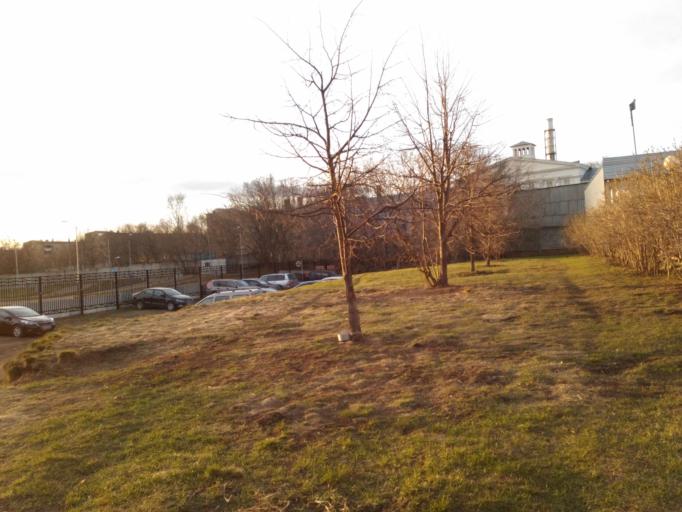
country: RU
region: Moskovskaya
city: Khoroshevo-Mnevniki
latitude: 55.7902
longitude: 37.4601
